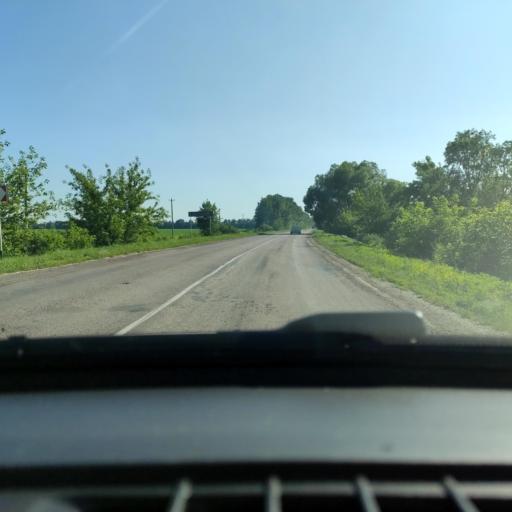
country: RU
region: Voronezj
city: Panino
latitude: 51.5958
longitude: 39.9753
